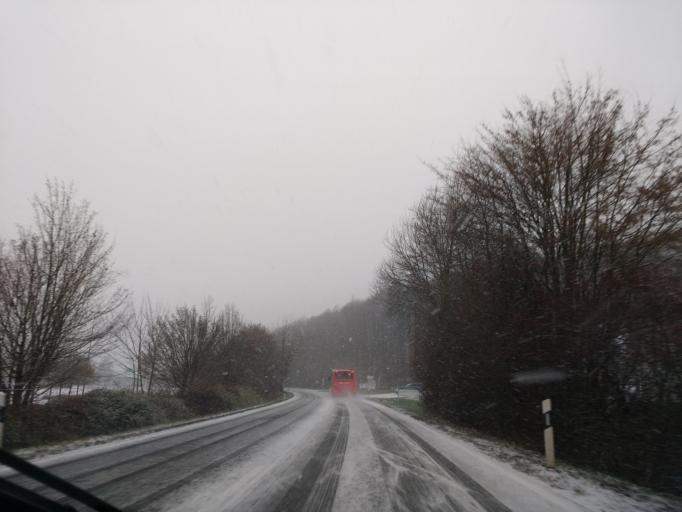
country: DE
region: Hesse
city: Melsungen
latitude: 51.1116
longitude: 9.5577
